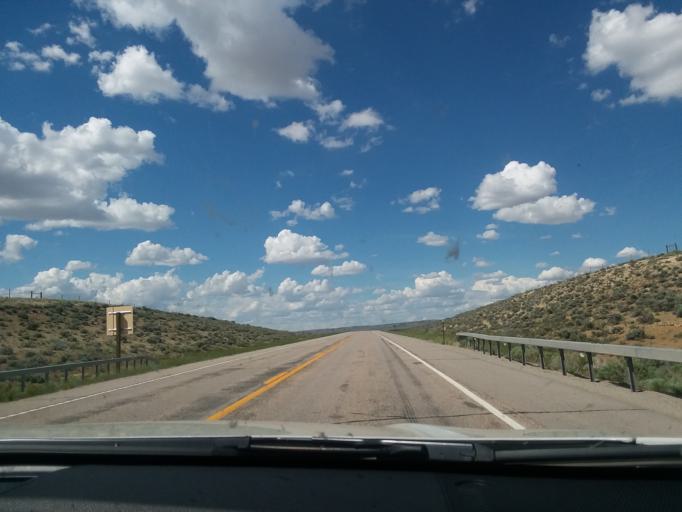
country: US
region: Wyoming
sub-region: Sweetwater County
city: North Rock Springs
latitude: 41.7772
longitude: -109.3381
